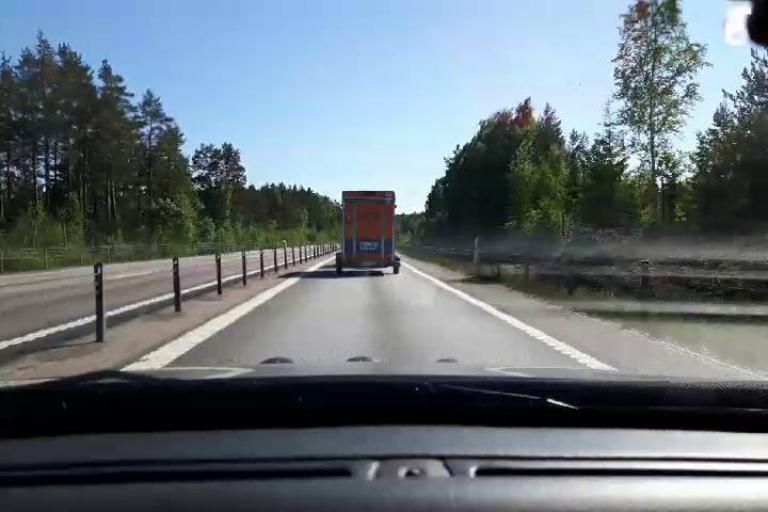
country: SE
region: Gaevleborg
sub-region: Soderhamns Kommun
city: Ljusne
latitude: 61.1446
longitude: 17.0318
